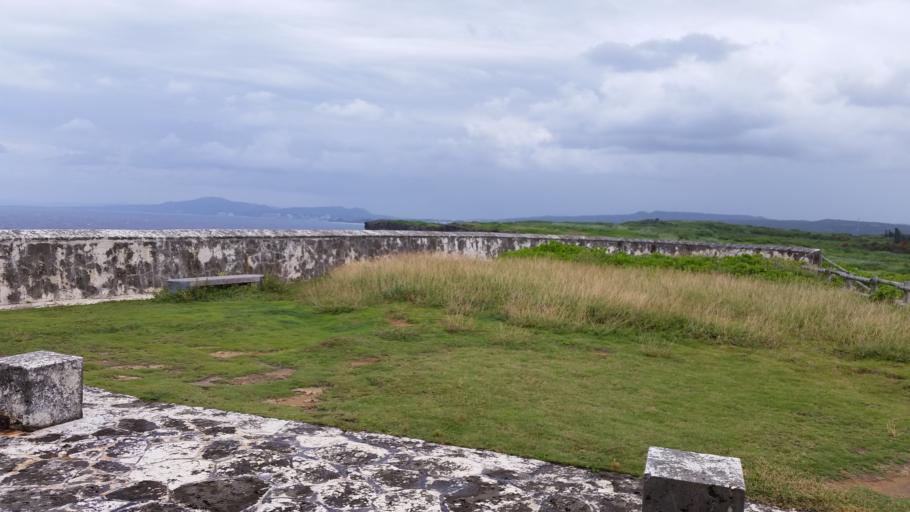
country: JP
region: Okinawa
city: Ishikawa
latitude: 26.4399
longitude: 127.7186
